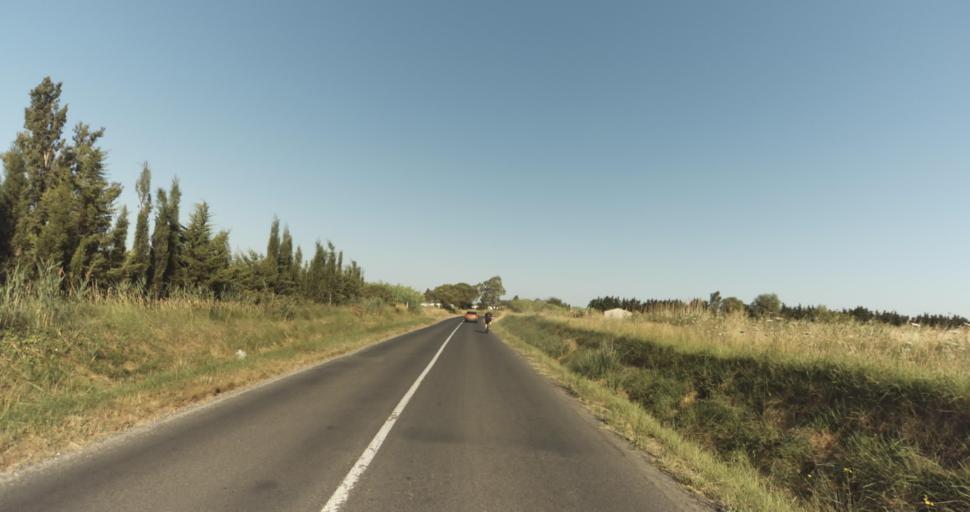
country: FR
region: Languedoc-Roussillon
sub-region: Departement des Pyrenees-Orientales
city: Alenya
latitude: 42.6363
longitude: 2.9968
